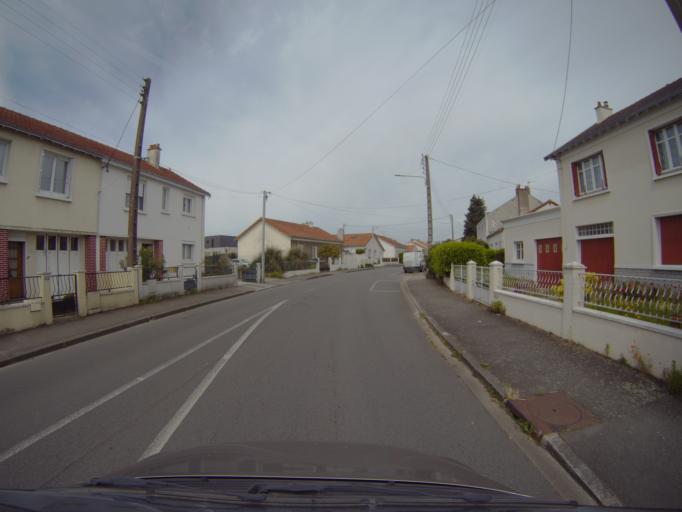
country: FR
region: Pays de la Loire
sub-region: Departement de la Loire-Atlantique
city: Reze
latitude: 47.1694
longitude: -1.5471
